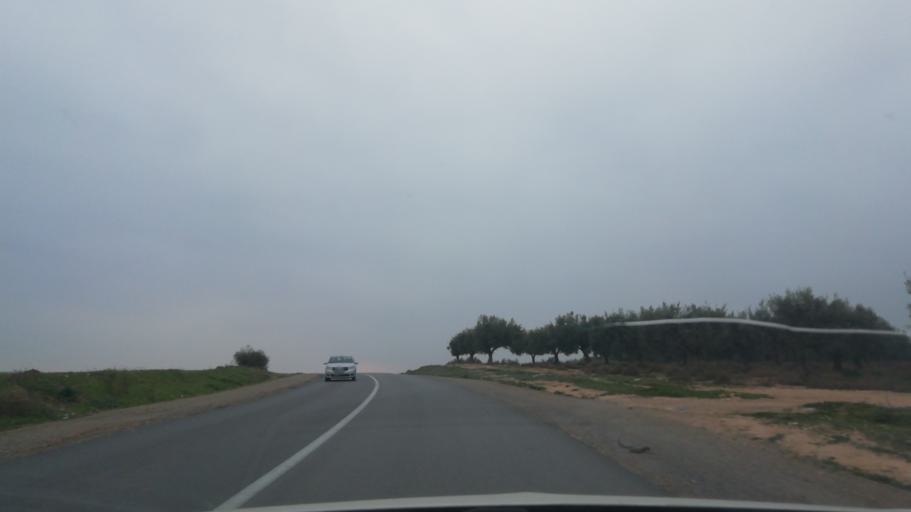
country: DZ
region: Sidi Bel Abbes
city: Sfizef
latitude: 35.2806
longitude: -0.1504
